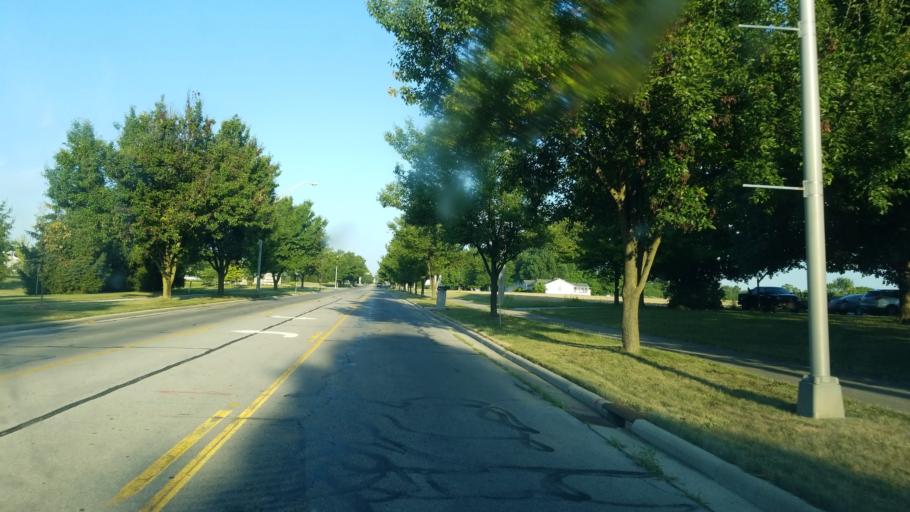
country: US
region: Ohio
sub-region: Franklin County
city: Hilliard
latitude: 40.0489
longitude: -83.1456
